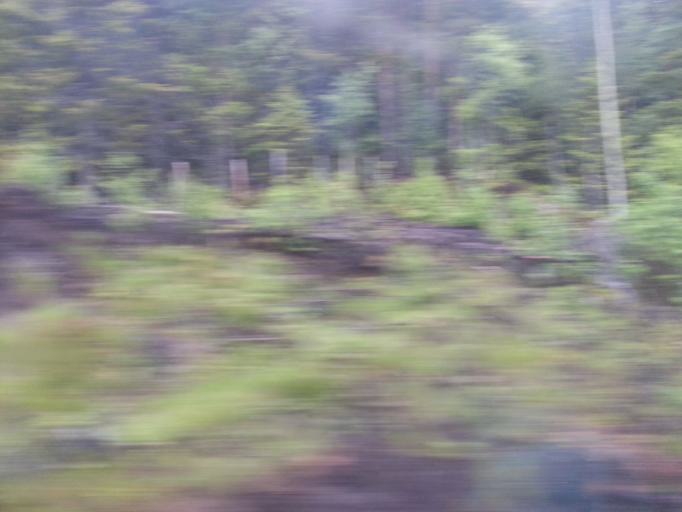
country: NO
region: Sor-Trondelag
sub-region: Rennebu
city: Berkak
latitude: 62.7685
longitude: 9.9906
